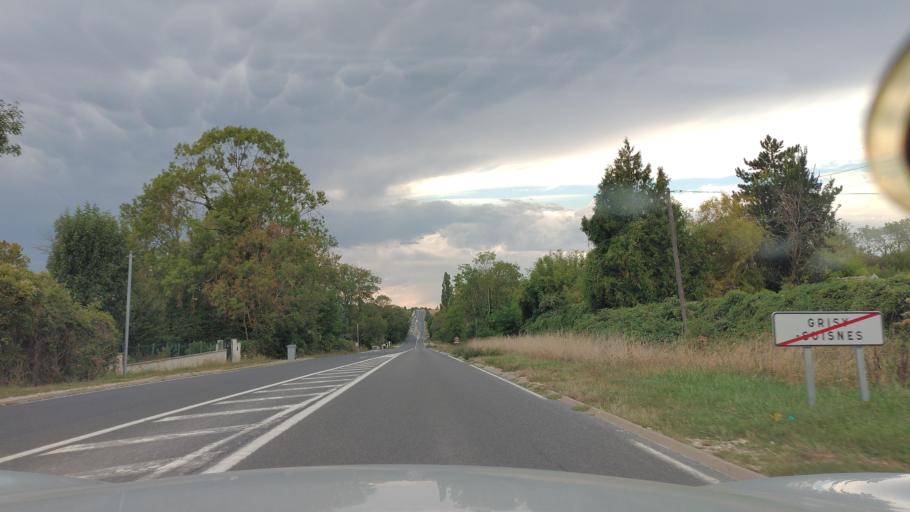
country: FR
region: Ile-de-France
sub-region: Departement de Seine-et-Marne
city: Grisy-Suisnes
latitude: 48.6794
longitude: 2.6547
